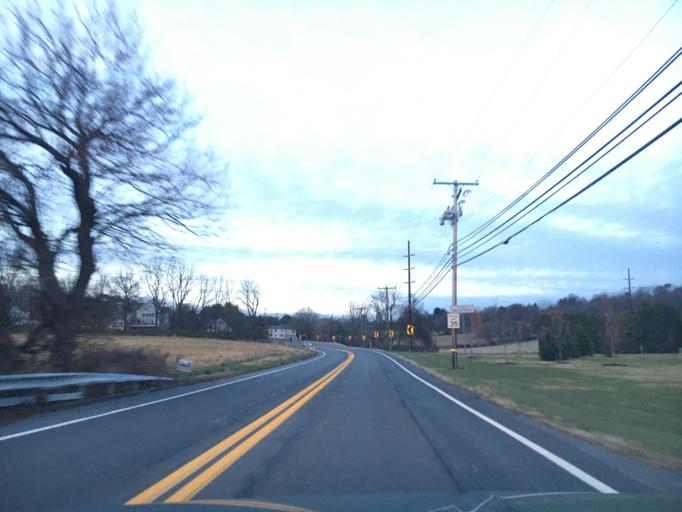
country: US
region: Pennsylvania
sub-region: Lehigh County
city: Schnecksville
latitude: 40.6728
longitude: -75.5684
